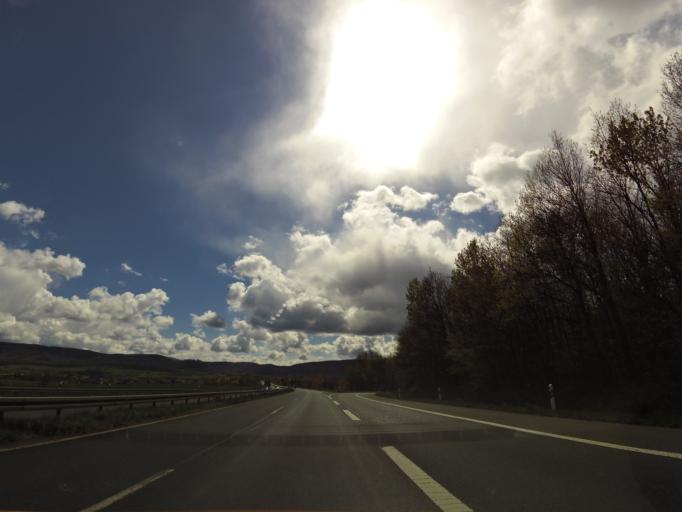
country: DE
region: Lower Saxony
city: Bad Harzburg
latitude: 51.9148
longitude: 10.5540
